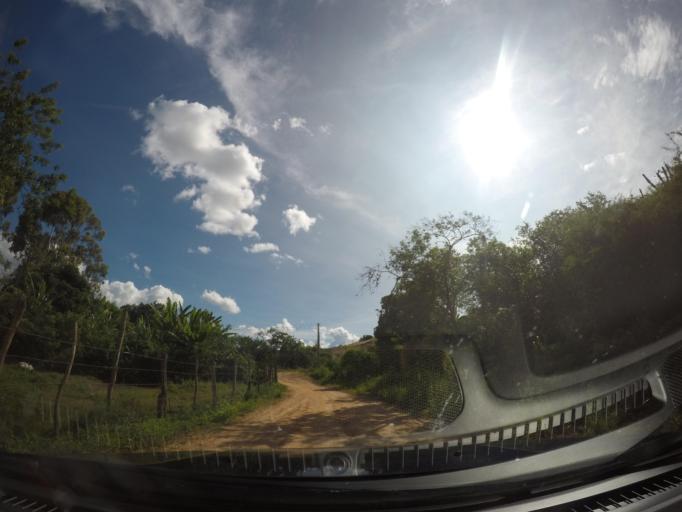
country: BR
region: Bahia
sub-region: Barra Da Estiva
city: Barra da Estiva
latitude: -13.1958
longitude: -41.5887
